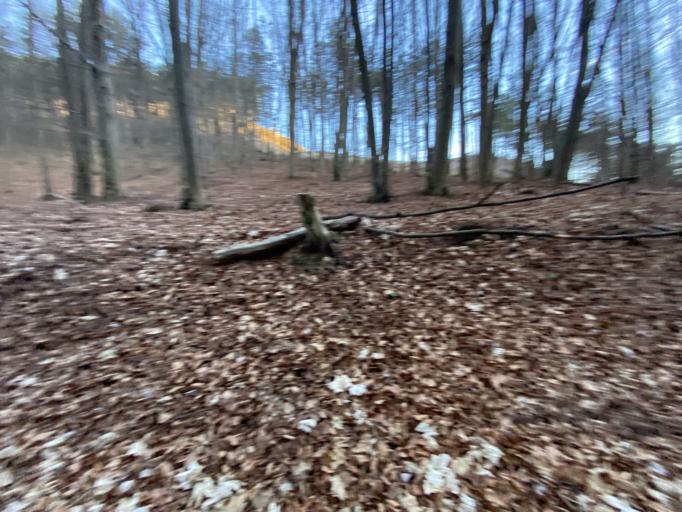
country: AT
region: Lower Austria
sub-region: Politischer Bezirk Baden
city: Hirtenberg
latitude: 47.9771
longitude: 16.1544
